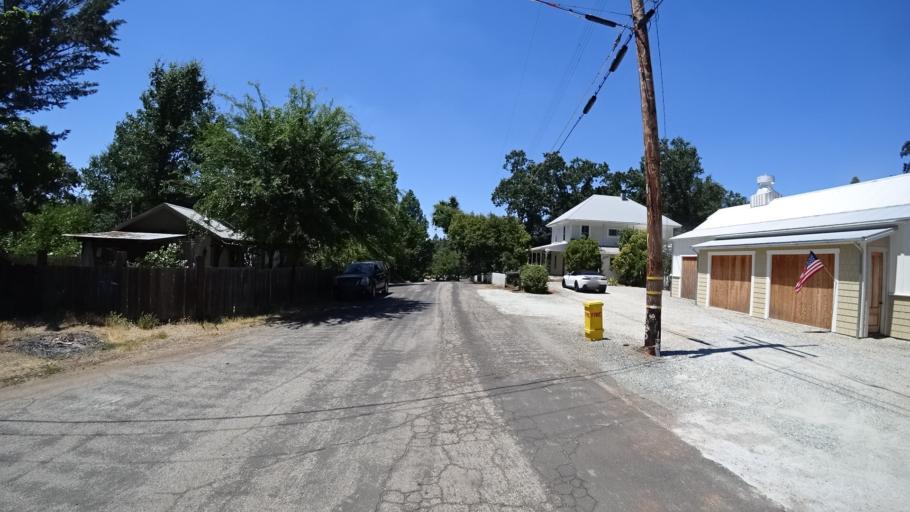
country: US
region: California
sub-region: Calaveras County
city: Murphys
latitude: 38.1370
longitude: -120.4546
